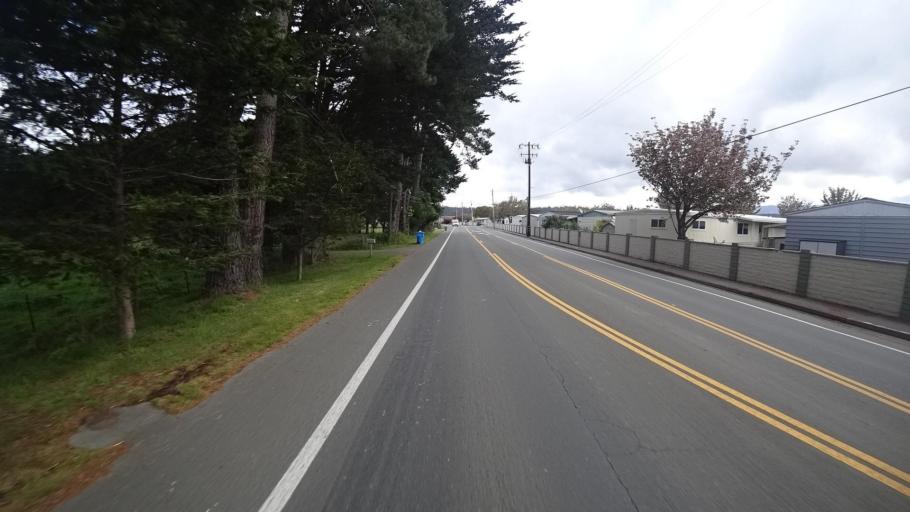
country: US
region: California
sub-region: Humboldt County
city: Arcata
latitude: 40.8995
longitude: -124.0920
